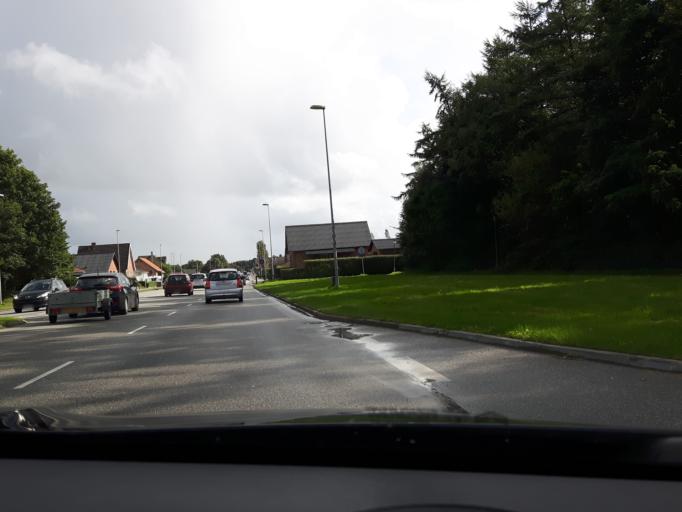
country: DK
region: Central Jutland
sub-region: Herning Kommune
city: Herning
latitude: 56.1421
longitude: 8.9426
